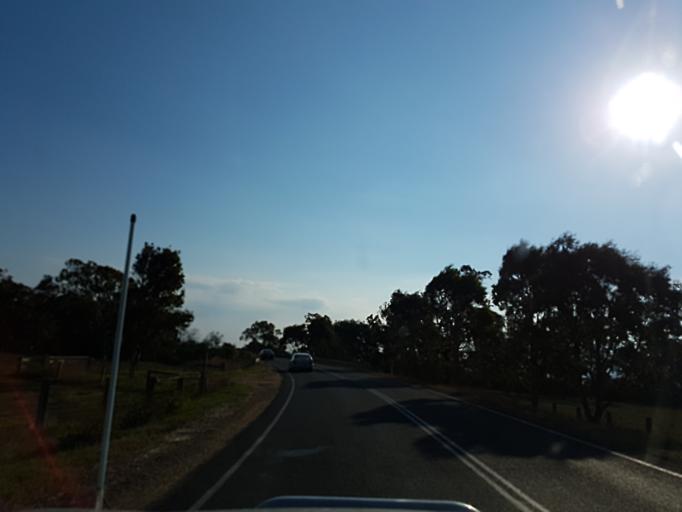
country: AU
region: Victoria
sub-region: Wellington
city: Sale
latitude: -38.0821
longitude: 147.0143
